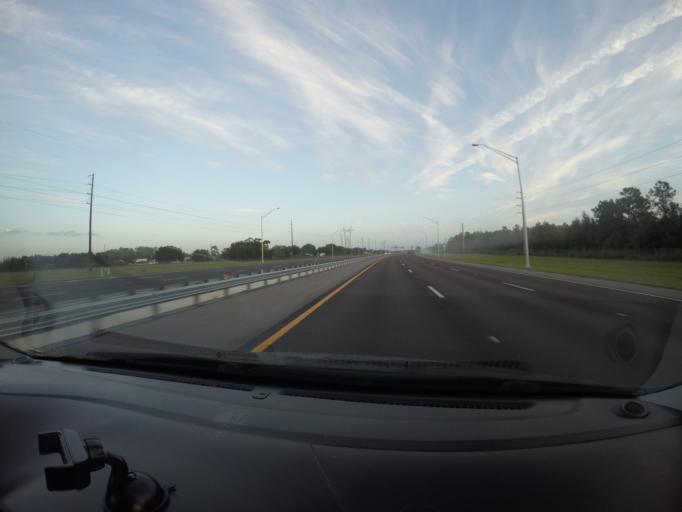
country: US
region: Florida
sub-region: Orange County
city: Azalea Park
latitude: 28.5177
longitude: -81.2506
